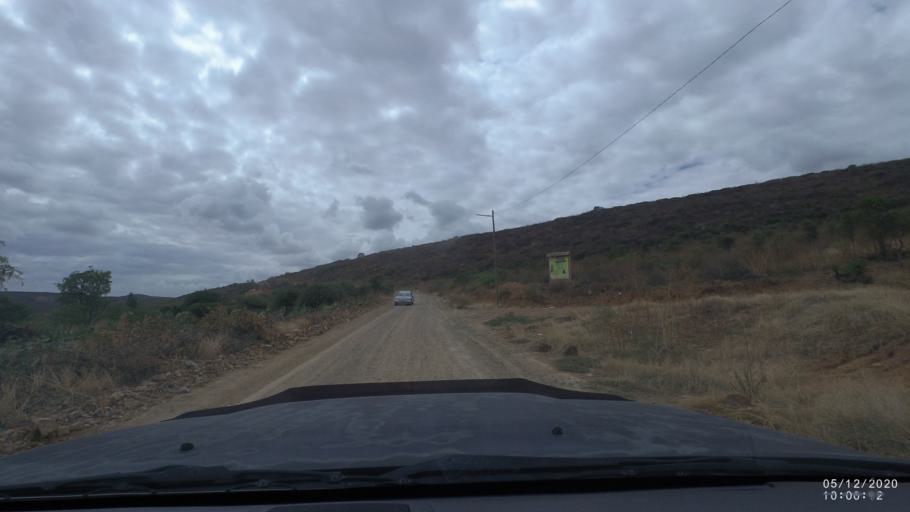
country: BO
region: Cochabamba
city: Sipe Sipe
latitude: -17.4364
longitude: -66.2899
